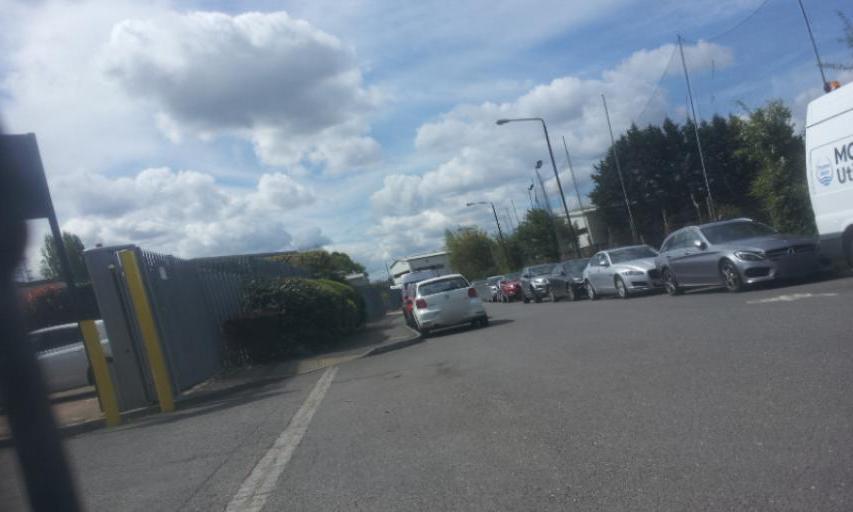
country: GB
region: England
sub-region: Greater London
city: Beckenham
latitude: 51.4212
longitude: -0.0365
